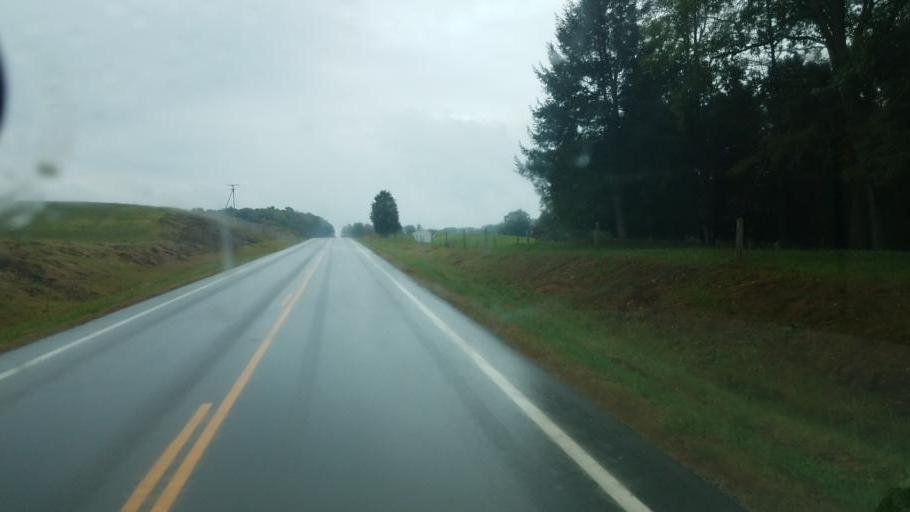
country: US
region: Ohio
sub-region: Richland County
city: Lincoln Heights
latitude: 40.6966
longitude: -82.3781
